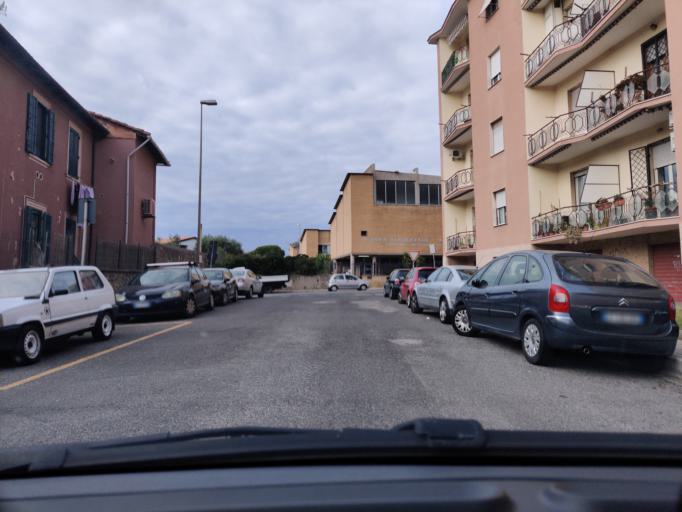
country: IT
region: Latium
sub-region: Citta metropolitana di Roma Capitale
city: Civitavecchia
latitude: 42.0962
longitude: 11.7987
